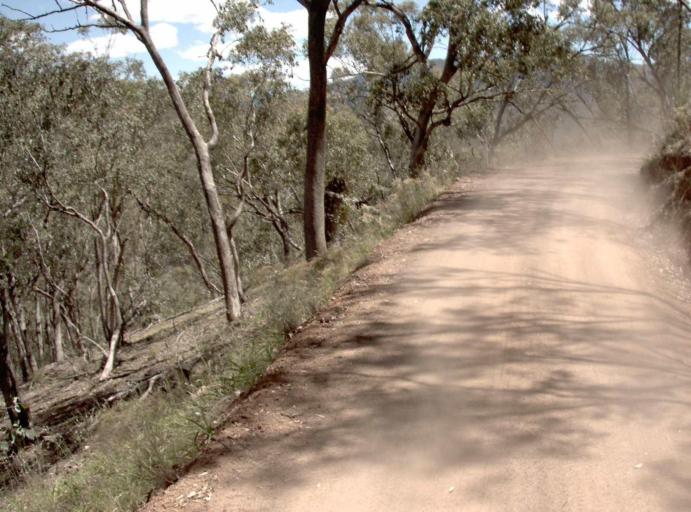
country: AU
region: New South Wales
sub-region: Snowy River
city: Jindabyne
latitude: -37.0864
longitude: 148.4020
